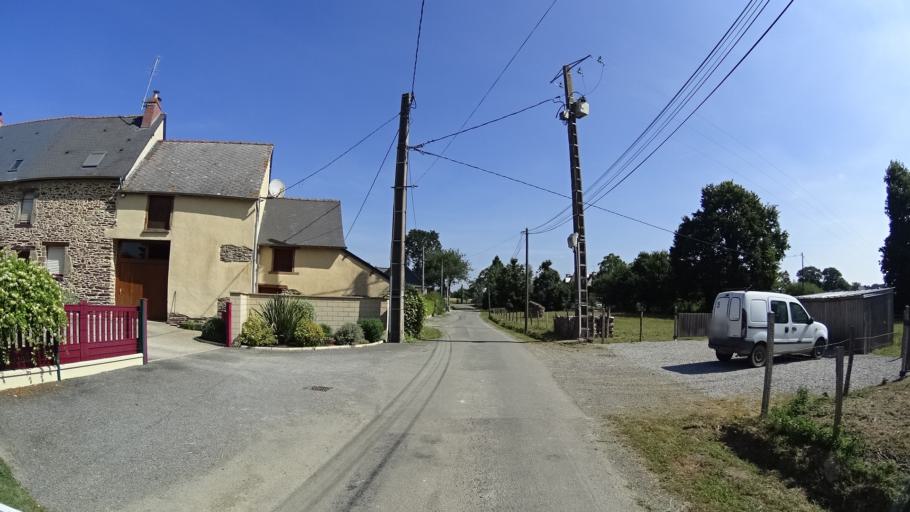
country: FR
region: Brittany
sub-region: Departement d'Ille-et-Vilaine
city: Orgeres
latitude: 47.9814
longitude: -1.6461
